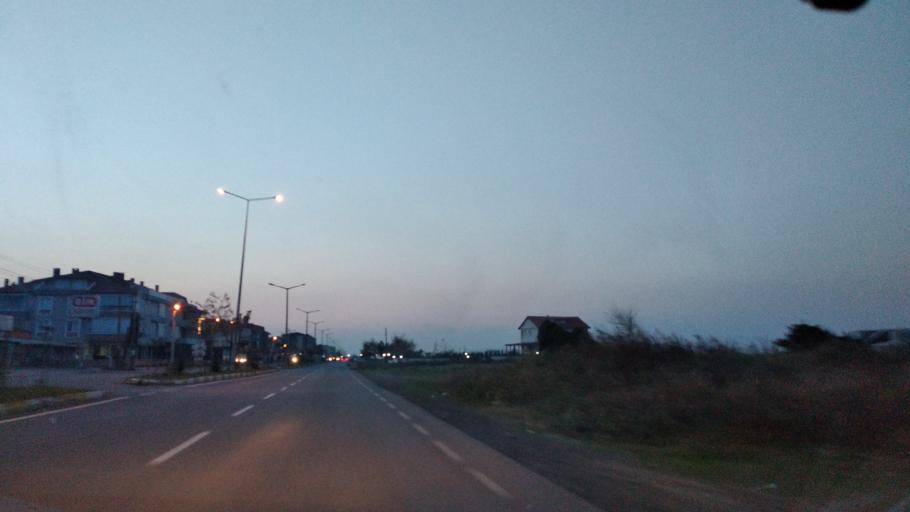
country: TR
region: Sakarya
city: Karasu
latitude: 41.0981
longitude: 30.7255
